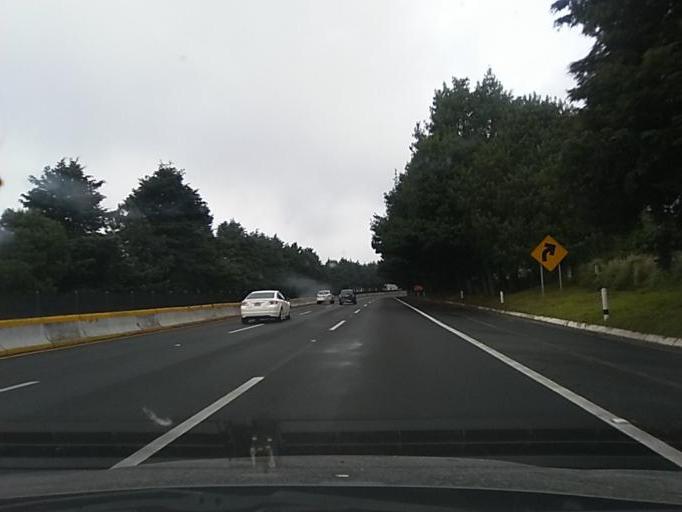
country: MX
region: Mexico City
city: Xochimilco
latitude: 19.1727
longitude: -99.1510
